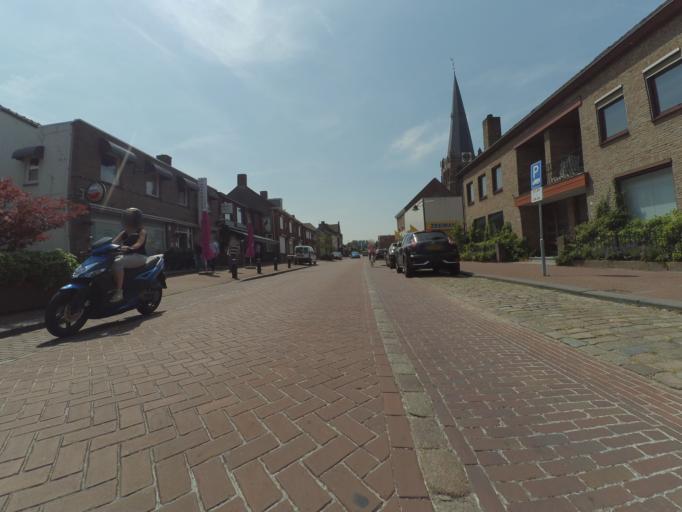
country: NL
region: North Brabant
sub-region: Gemeente Woensdrecht
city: Woensdrecht
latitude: 51.4237
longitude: 4.3235
